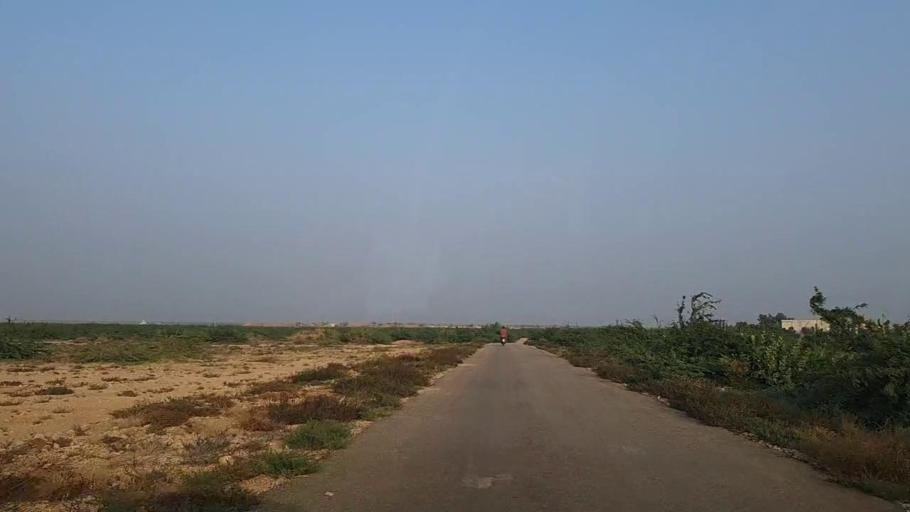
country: PK
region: Sindh
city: Thatta
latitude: 24.6908
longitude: 67.8427
